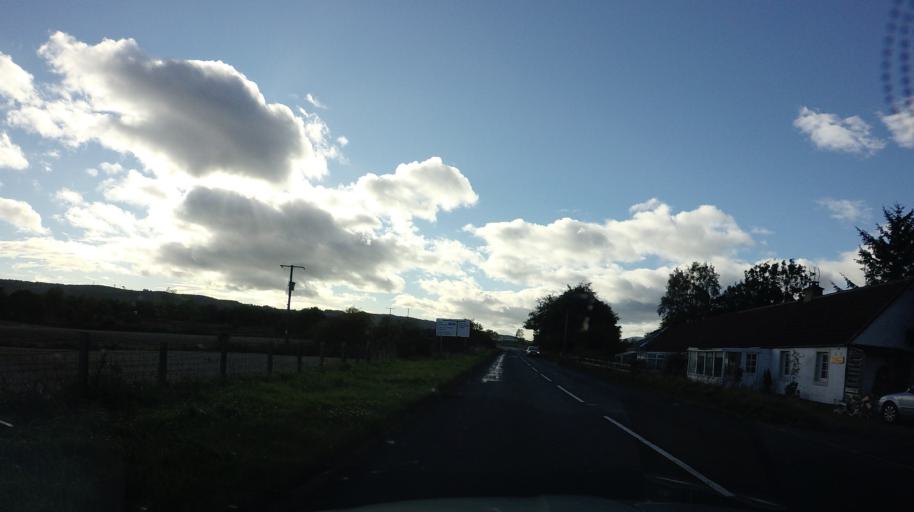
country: GB
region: Scotland
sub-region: Fife
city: Kelty
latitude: 56.1700
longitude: -3.3985
